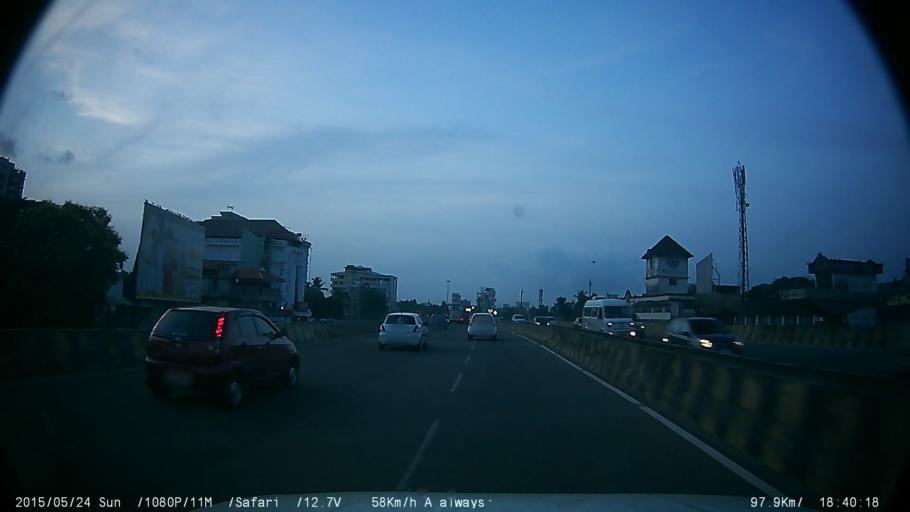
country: IN
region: Kerala
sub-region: Ernakulam
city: Aluva
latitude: 10.1064
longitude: 76.3499
